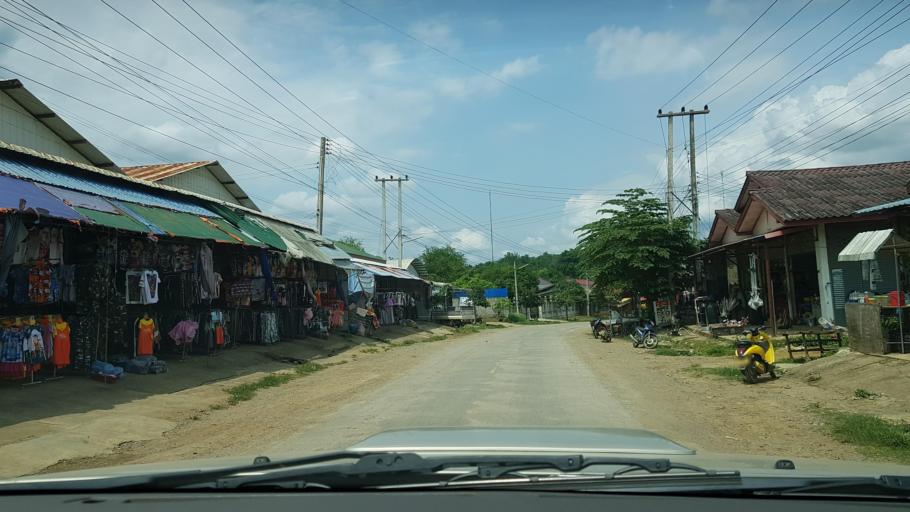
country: TH
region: Nan
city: Chaloem Phra Kiat
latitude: 20.0266
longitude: 101.3387
